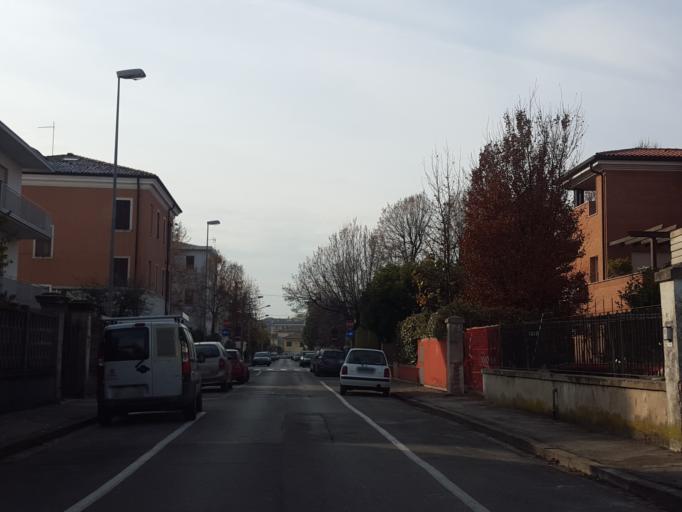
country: IT
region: Veneto
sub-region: Provincia di Vicenza
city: Vicenza
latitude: 45.5564
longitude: 11.5397
